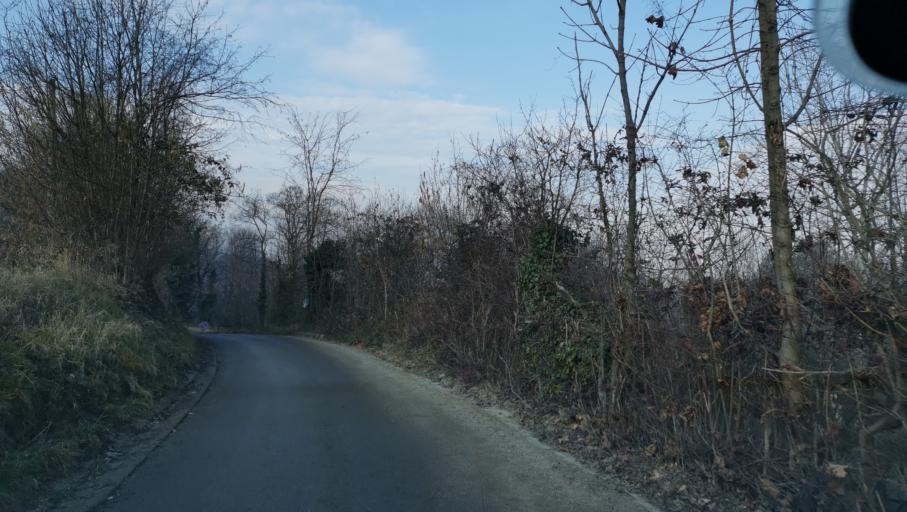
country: IT
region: Piedmont
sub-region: Provincia di Torino
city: Gassino Torinese
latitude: 45.1154
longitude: 7.8351
